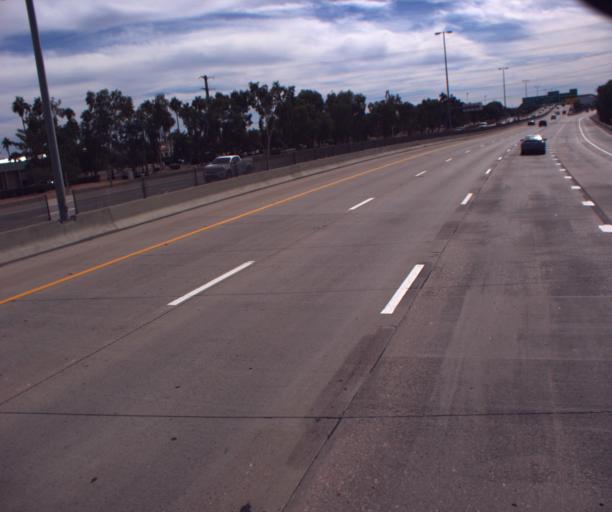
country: US
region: Arizona
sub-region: Maricopa County
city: Tempe Junction
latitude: 33.4289
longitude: -111.9781
